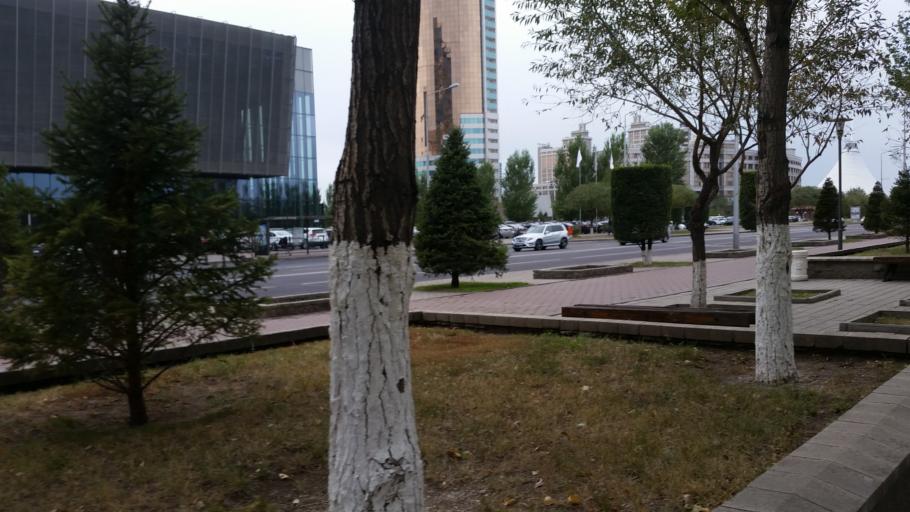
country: KZ
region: Astana Qalasy
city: Astana
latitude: 51.1326
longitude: 71.4198
